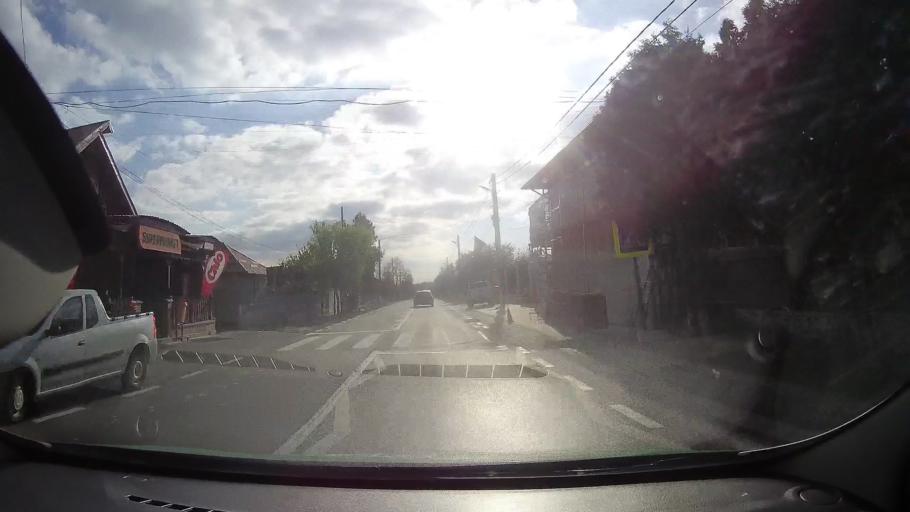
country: RO
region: Tulcea
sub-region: Comuna Topolog
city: Topolog
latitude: 44.8780
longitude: 28.3750
